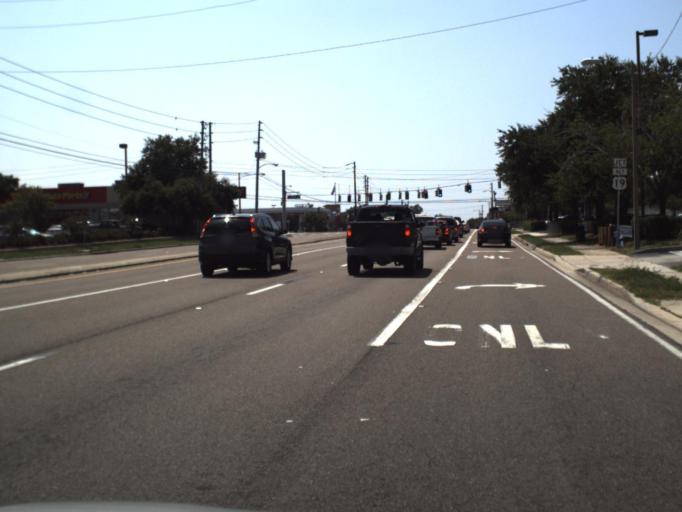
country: US
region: Florida
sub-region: Pinellas County
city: Seminole
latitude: 27.8397
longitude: -82.7854
